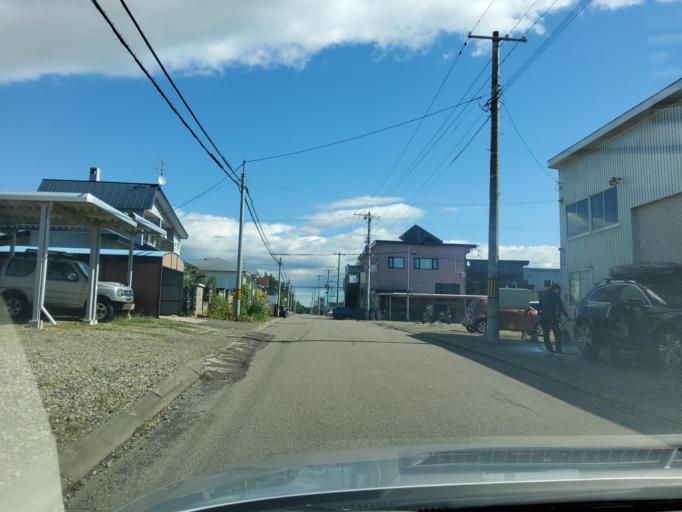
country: JP
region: Hokkaido
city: Obihiro
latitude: 42.9491
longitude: 143.1970
